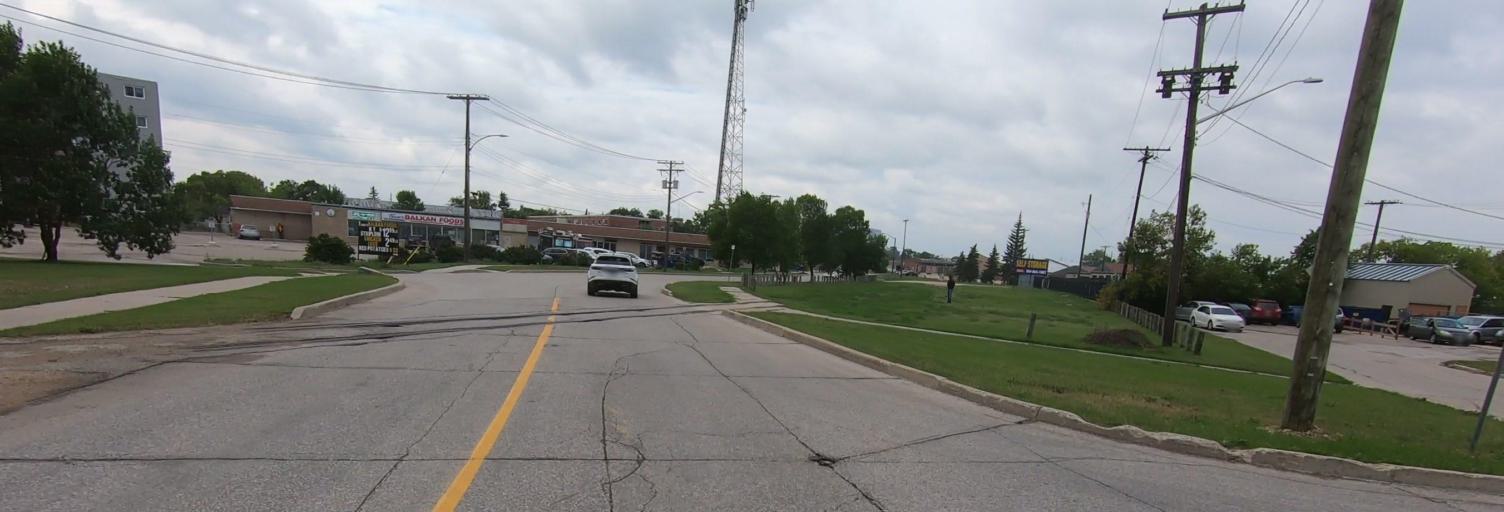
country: CA
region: Manitoba
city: Winnipeg
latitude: 49.9107
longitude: -97.1060
